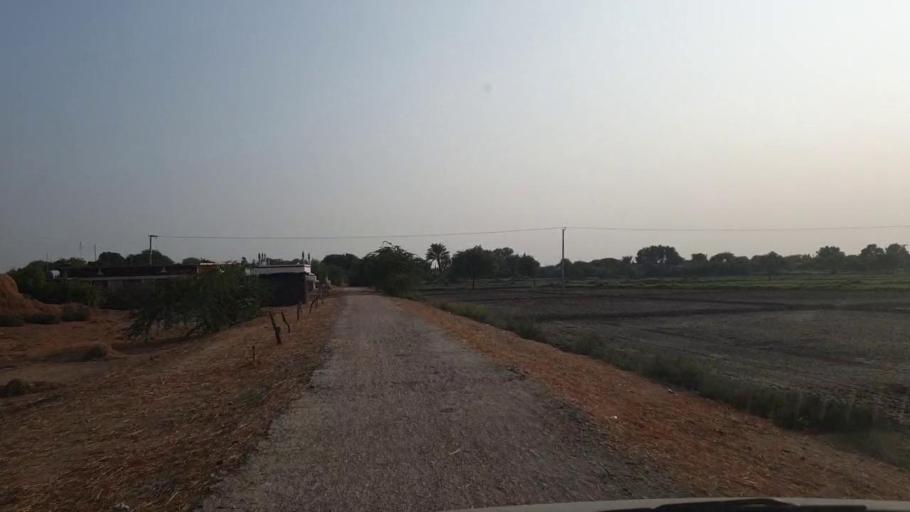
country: PK
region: Sindh
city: Rajo Khanani
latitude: 25.0342
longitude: 68.7771
